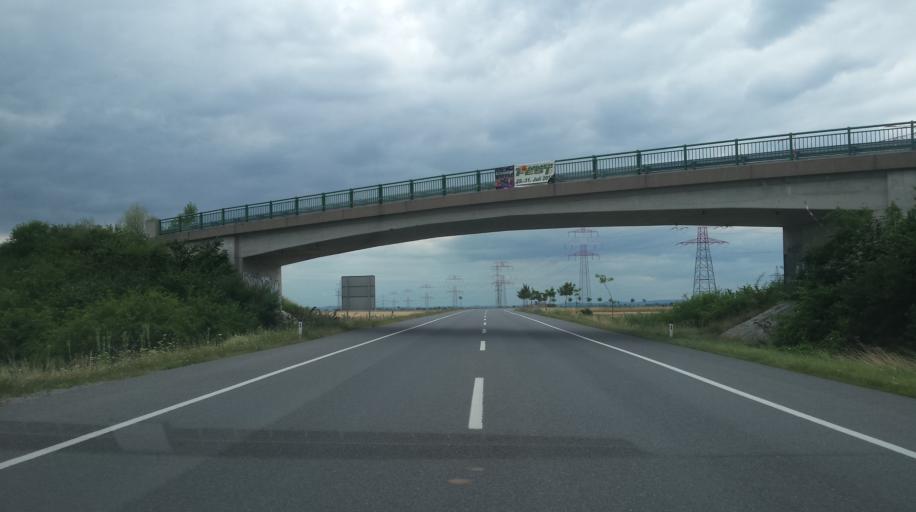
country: AT
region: Lower Austria
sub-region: Politischer Bezirk Wien-Umgebung
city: Himberg
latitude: 48.0810
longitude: 16.4597
